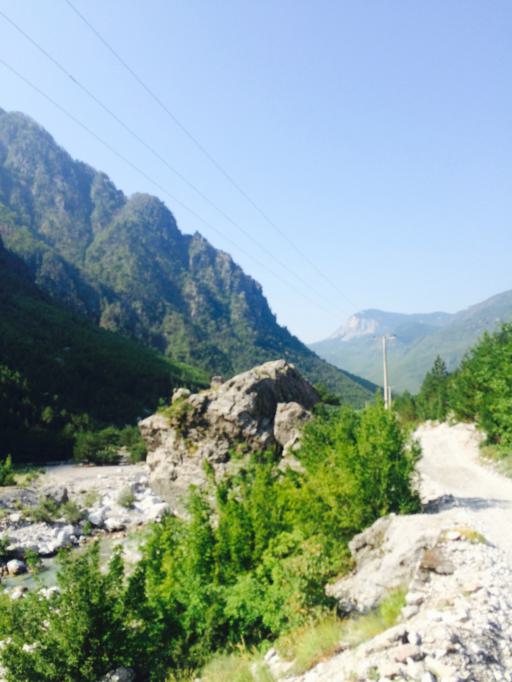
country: AL
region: Shkoder
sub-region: Rrethi i Shkodres
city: Nicaj-Shale
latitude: 42.3610
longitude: 19.7841
